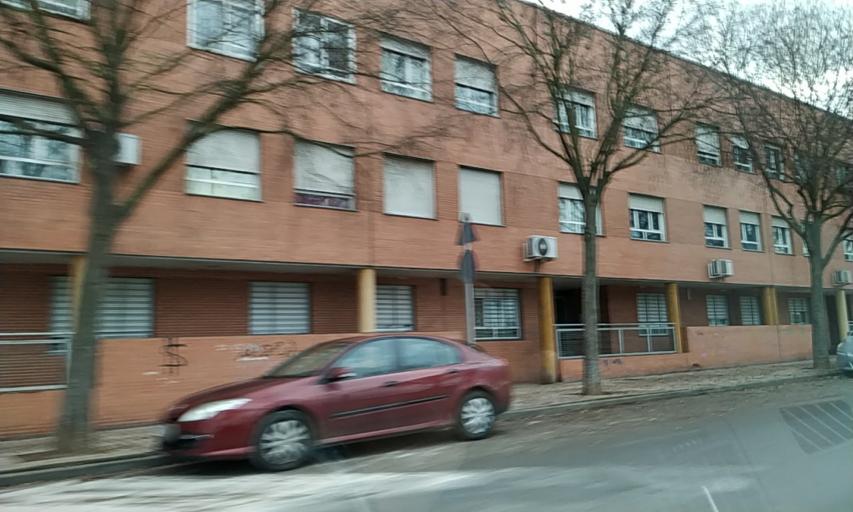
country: ES
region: Extremadura
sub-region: Provincia de Badajoz
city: Badajoz
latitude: 38.8826
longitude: -6.9600
